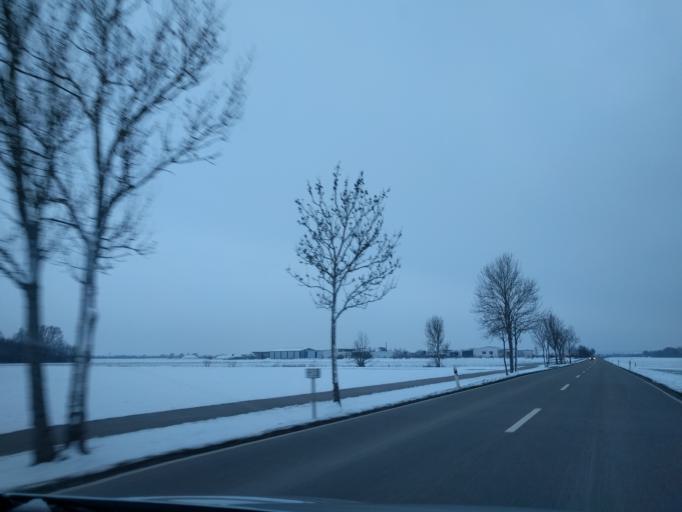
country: DE
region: Bavaria
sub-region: Swabia
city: Genderkingen
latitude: 48.7091
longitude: 10.8696
